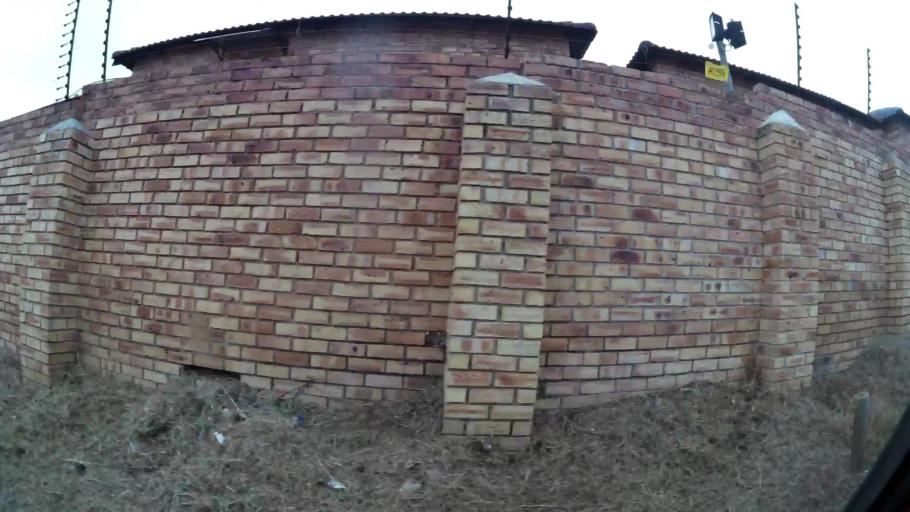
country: ZA
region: Gauteng
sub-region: City of Johannesburg Metropolitan Municipality
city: Roodepoort
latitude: -26.1115
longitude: 27.9007
